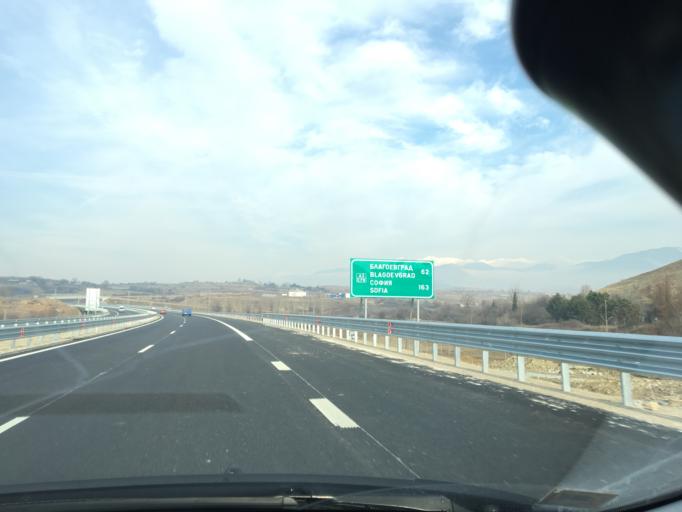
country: BG
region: Blagoevgrad
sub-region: Obshtina Sandanski
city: Sandanski
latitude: 41.5178
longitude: 23.2718
